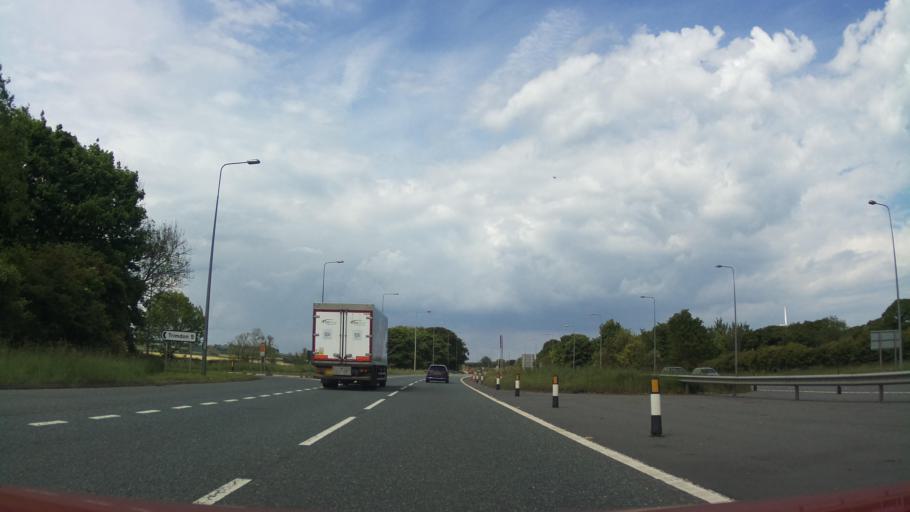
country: GB
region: England
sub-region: Hartlepool
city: Elwick
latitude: 54.6797
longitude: -1.3017
